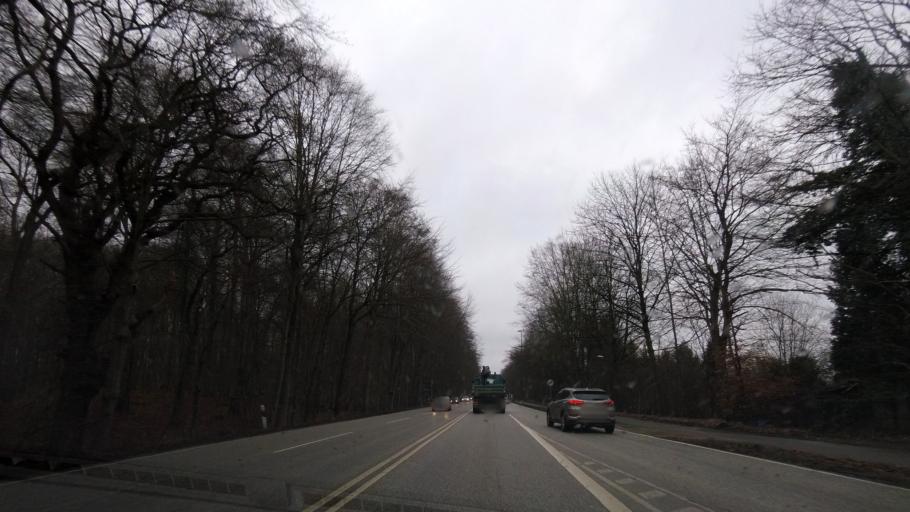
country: DE
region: Schleswig-Holstein
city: Kiel
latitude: 54.2951
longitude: 10.1267
